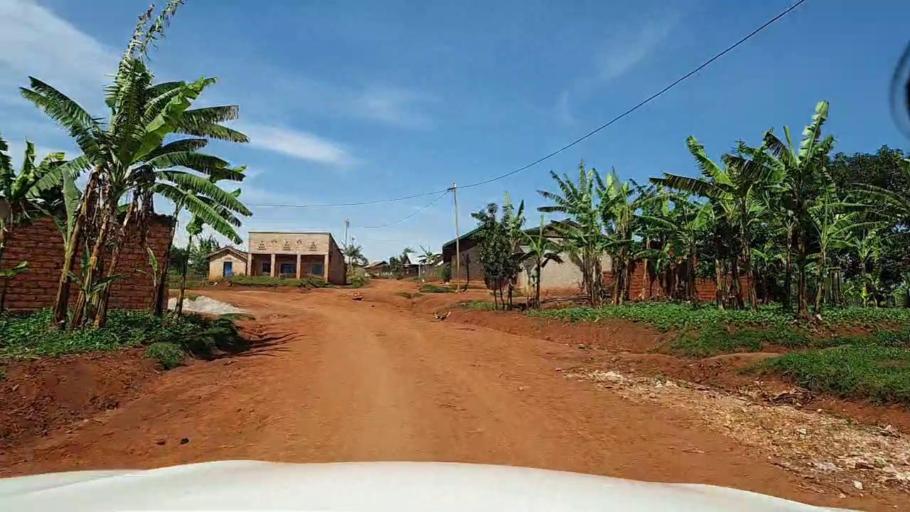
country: RW
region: Southern Province
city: Butare
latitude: -2.7025
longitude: 29.8469
